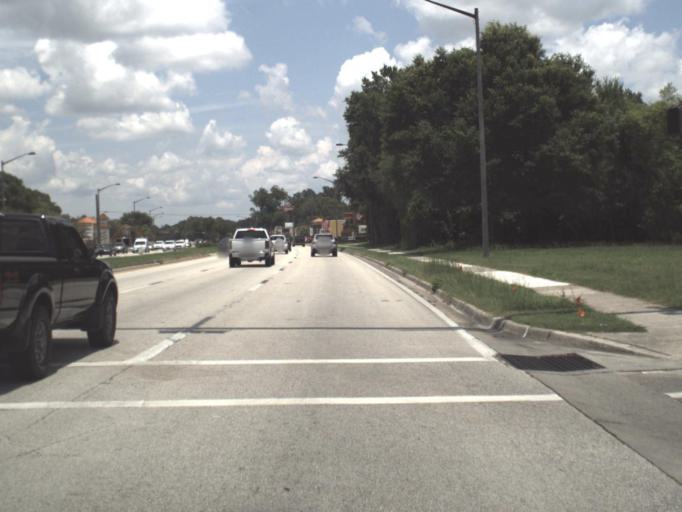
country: US
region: Florida
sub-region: Alachua County
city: Gainesville
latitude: 29.6203
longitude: -82.3801
